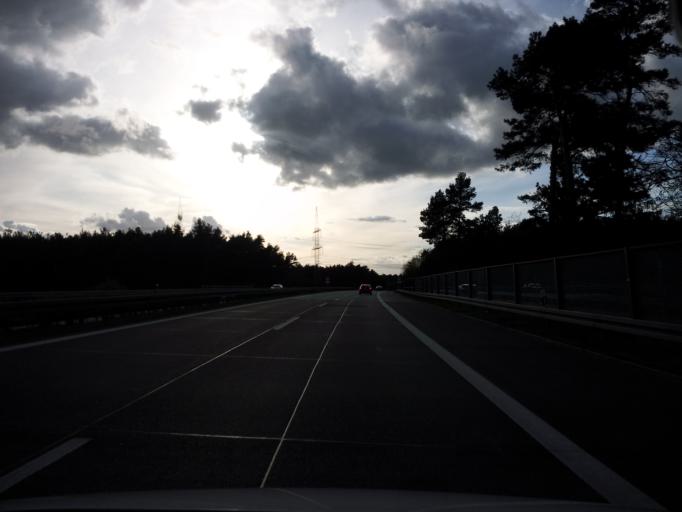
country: DE
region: Brandenburg
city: Kolkwitz
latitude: 51.7288
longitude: 14.1904
